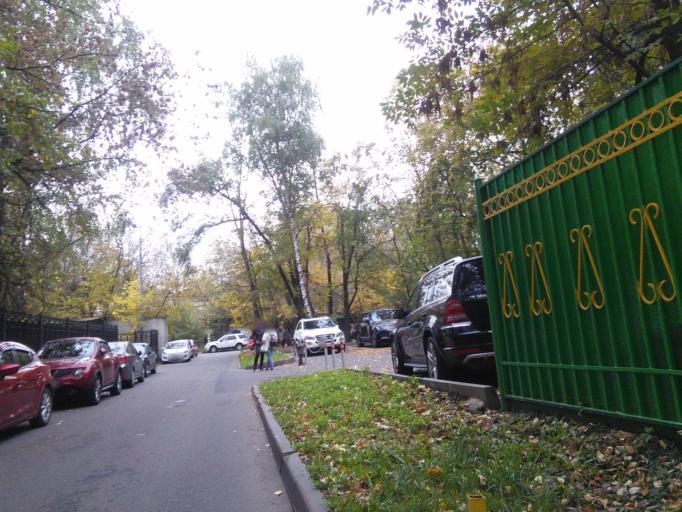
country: RU
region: Moscow
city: Novyye Cheremushki
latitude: 55.7019
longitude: 37.5757
